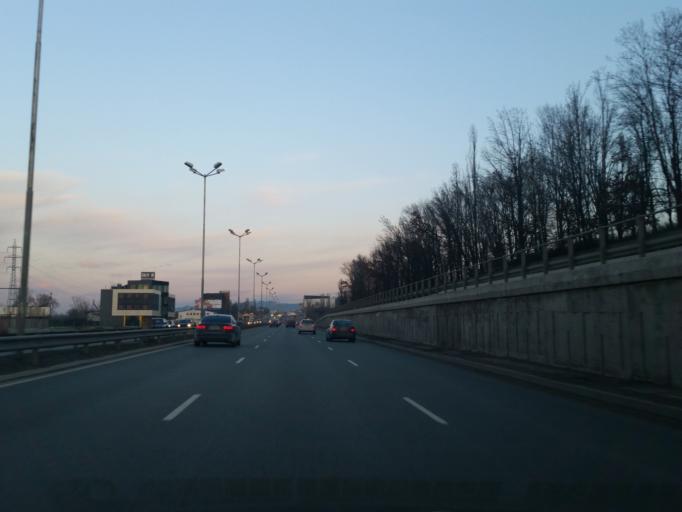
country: BG
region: Sofia-Capital
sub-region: Stolichna Obshtina
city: Sofia
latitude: 42.6472
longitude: 23.2988
